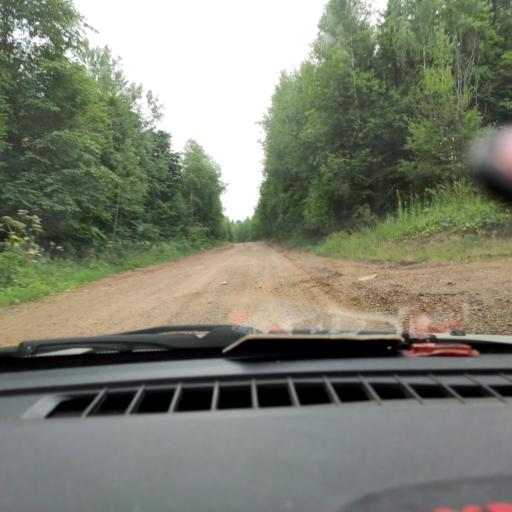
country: RU
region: Perm
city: Kultayevo
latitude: 57.8065
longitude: 56.0040
